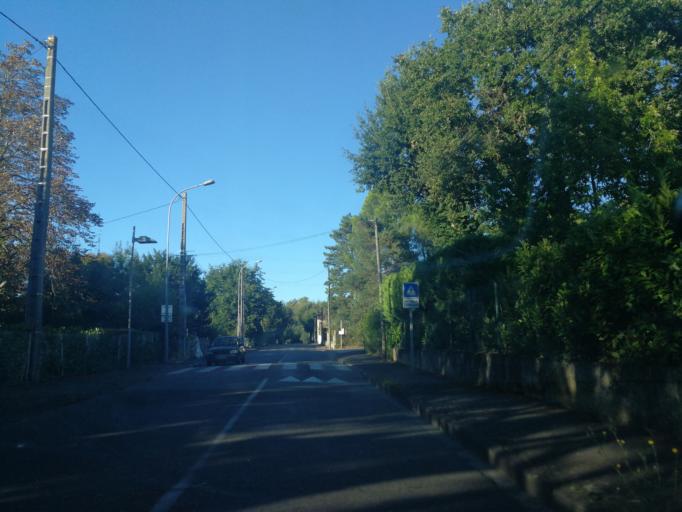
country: FR
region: Midi-Pyrenees
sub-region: Departement de la Haute-Garonne
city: Balma
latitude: 43.6142
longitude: 1.5029
